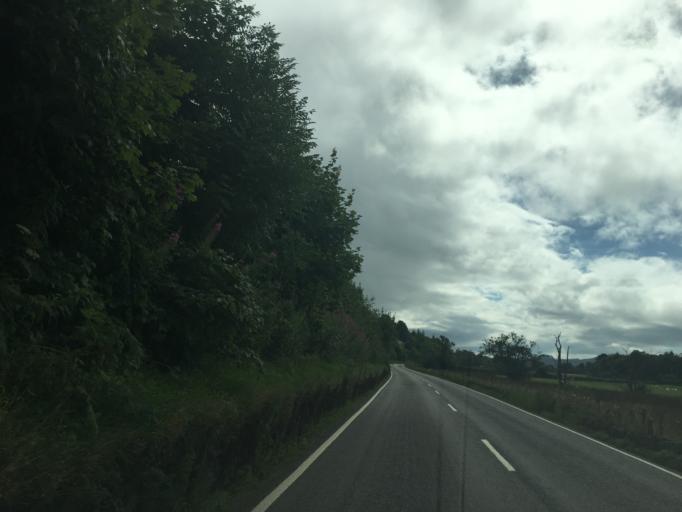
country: GB
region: Scotland
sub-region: Argyll and Bute
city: Lochgilphead
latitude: 56.1278
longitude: -5.4871
